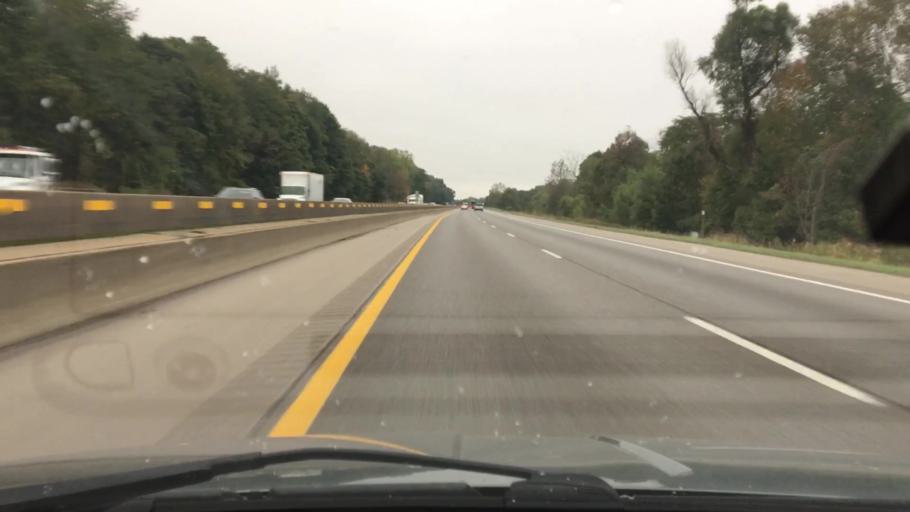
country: US
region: Michigan
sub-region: Kalamazoo County
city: Galesburg
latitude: 42.2695
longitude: -85.4599
